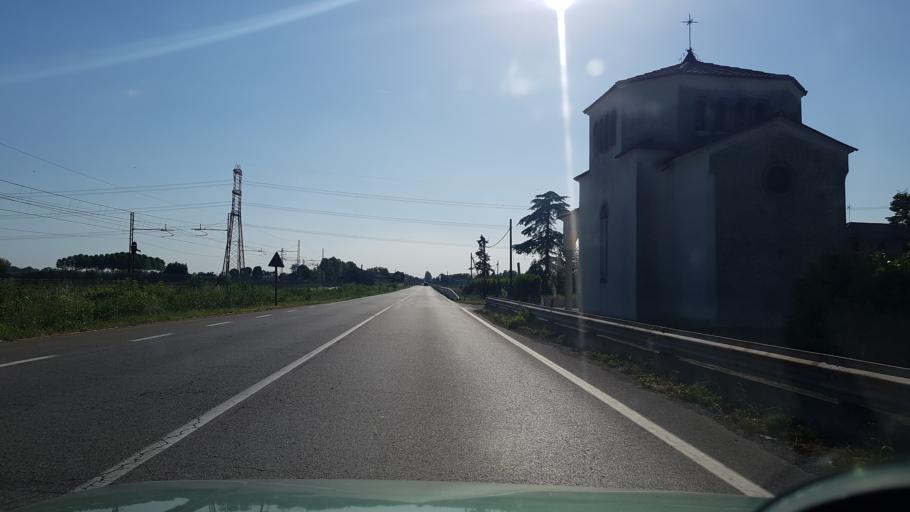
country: IT
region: Friuli Venezia Giulia
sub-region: Provincia di Udine
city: Torviscosa
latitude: 45.8280
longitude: 13.2493
